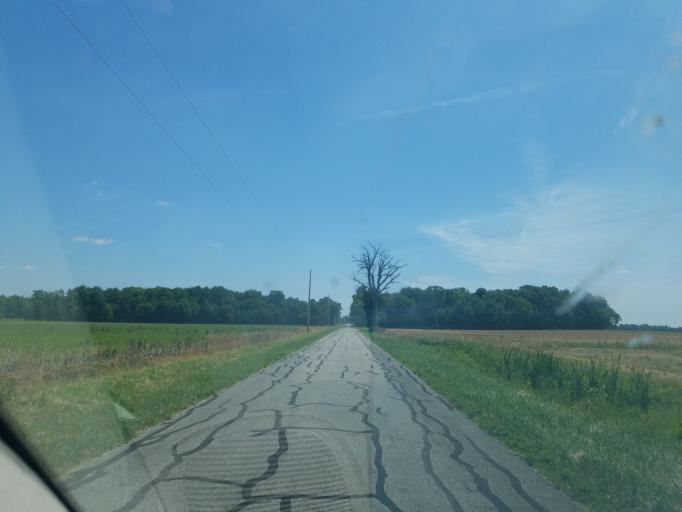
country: US
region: Ohio
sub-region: Hancock County
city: Arlington
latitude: 40.8630
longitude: -83.7240
